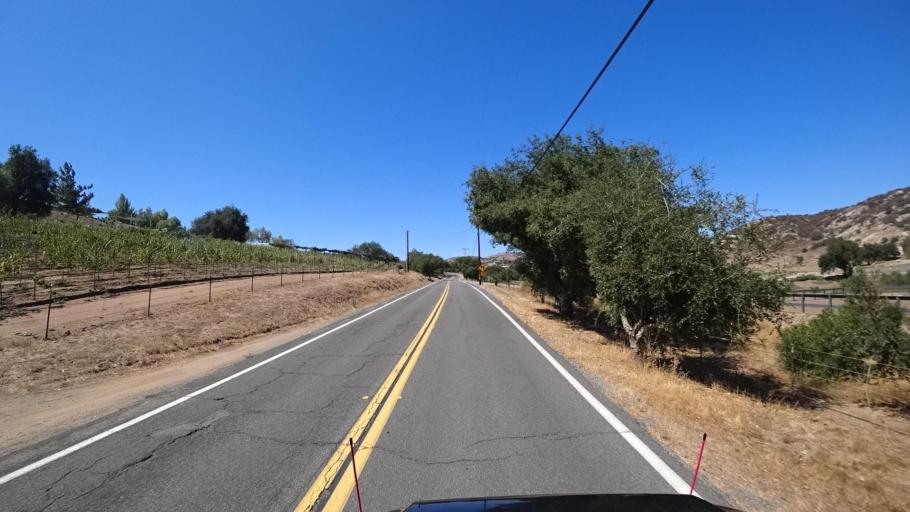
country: US
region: California
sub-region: San Diego County
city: San Diego Country Estates
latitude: 33.0498
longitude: -116.8094
